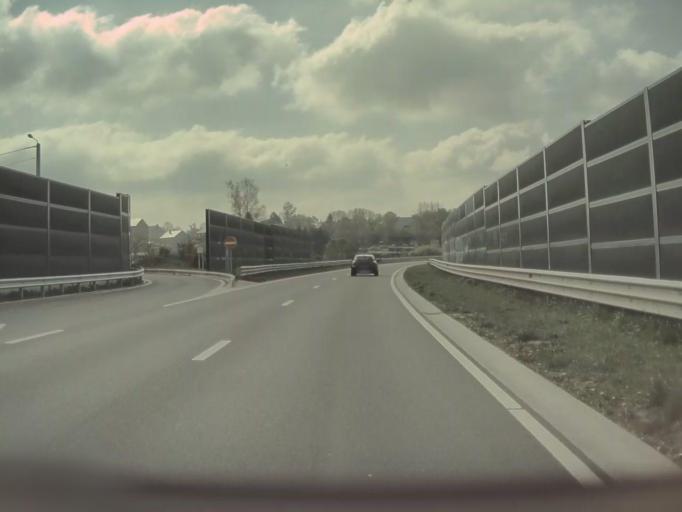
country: BE
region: Wallonia
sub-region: Province du Luxembourg
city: Marche-en-Famenne
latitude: 50.2302
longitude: 5.3130
